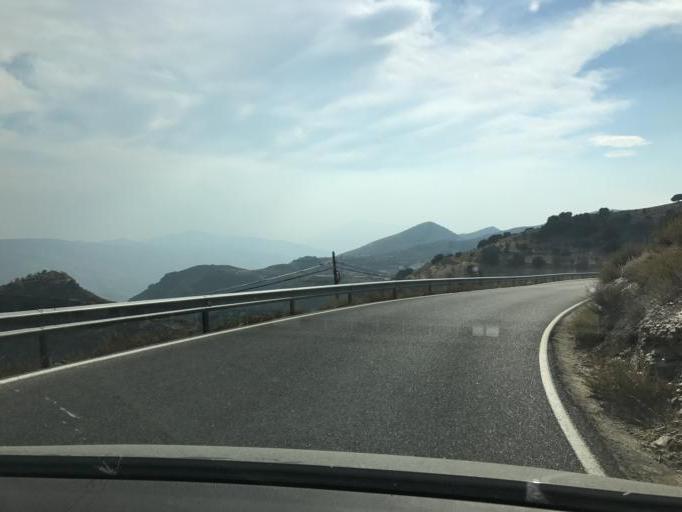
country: ES
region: Andalusia
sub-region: Provincia de Granada
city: Juviles
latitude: 36.9563
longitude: -3.2119
